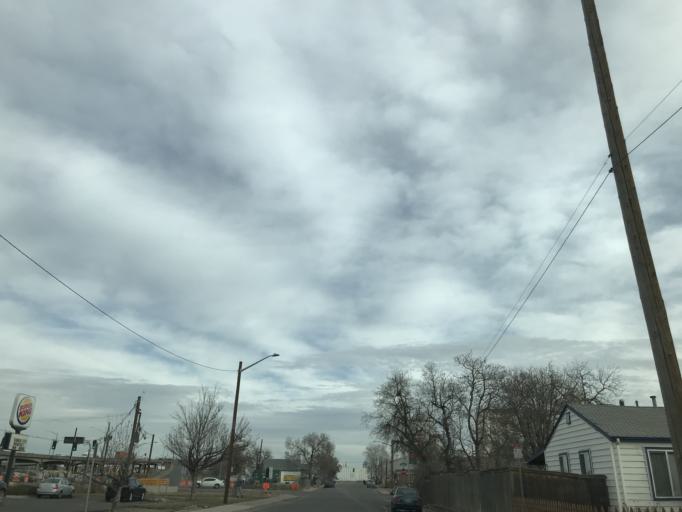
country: US
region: Colorado
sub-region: Adams County
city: Commerce City
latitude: 39.7789
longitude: -104.9509
